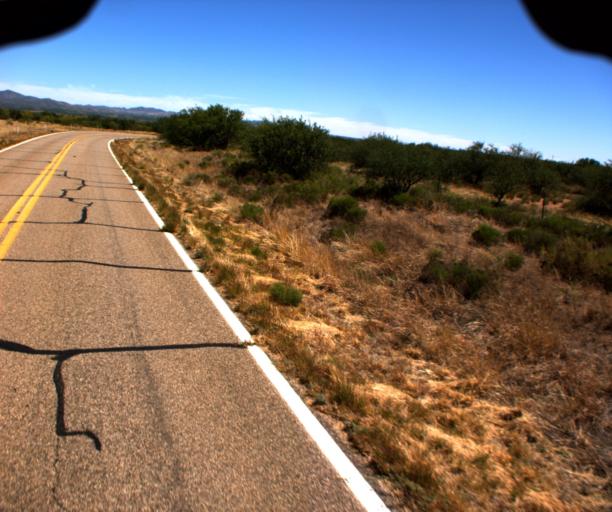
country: US
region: Arizona
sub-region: Pima County
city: Arivaca Junction
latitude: 31.6841
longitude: -111.4865
